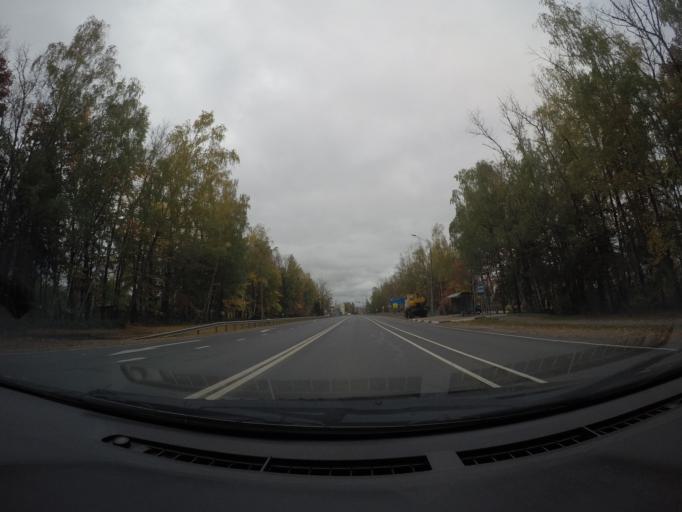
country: RU
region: Moskovskaya
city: Ruza
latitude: 55.7126
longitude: 36.2062
